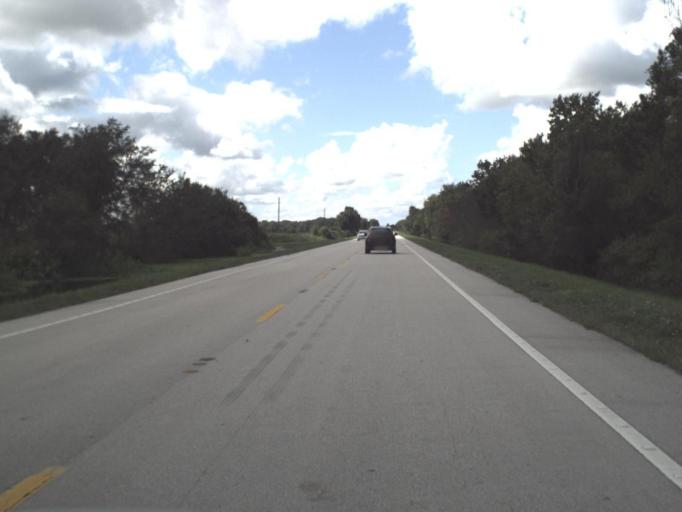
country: US
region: Florida
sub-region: DeSoto County
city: Arcadia
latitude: 27.2881
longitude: -82.0468
